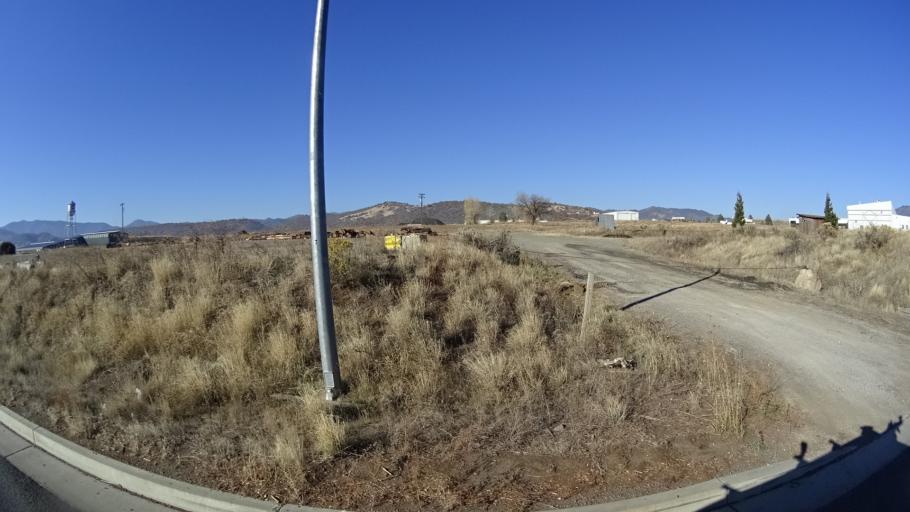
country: US
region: California
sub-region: Siskiyou County
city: Yreka
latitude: 41.7325
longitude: -122.5933
